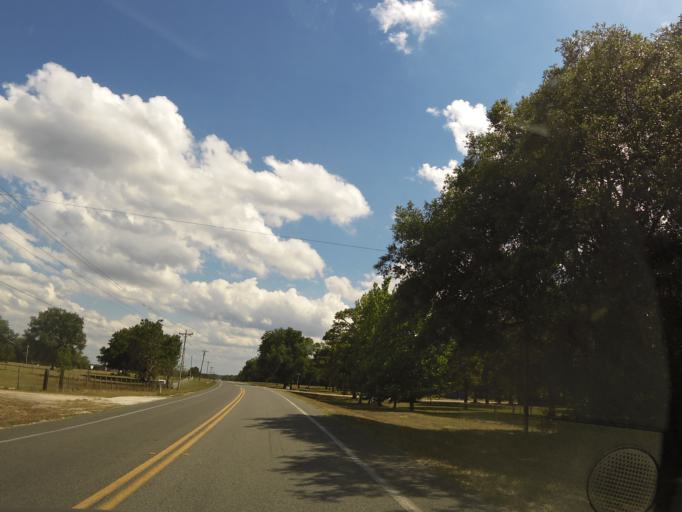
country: US
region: Florida
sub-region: Clay County
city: Keystone Heights
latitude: 29.8372
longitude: -81.9226
